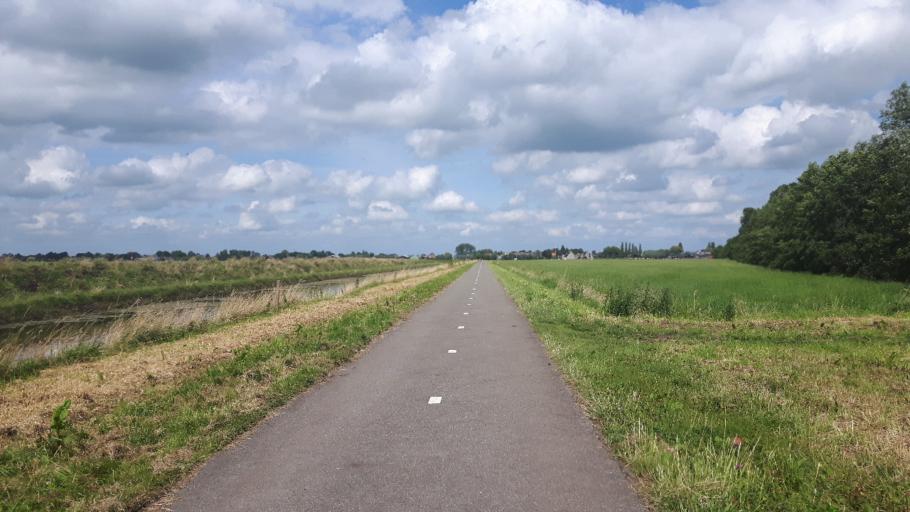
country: NL
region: South Holland
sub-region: Gemeente Vlist
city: Vlist
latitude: 51.9687
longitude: 4.8104
